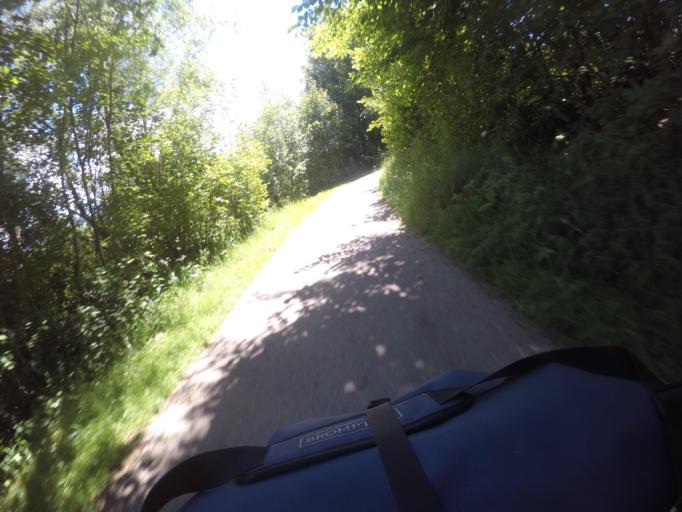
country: DE
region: Bavaria
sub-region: Swabia
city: Fuessen
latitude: 47.5774
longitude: 10.7126
